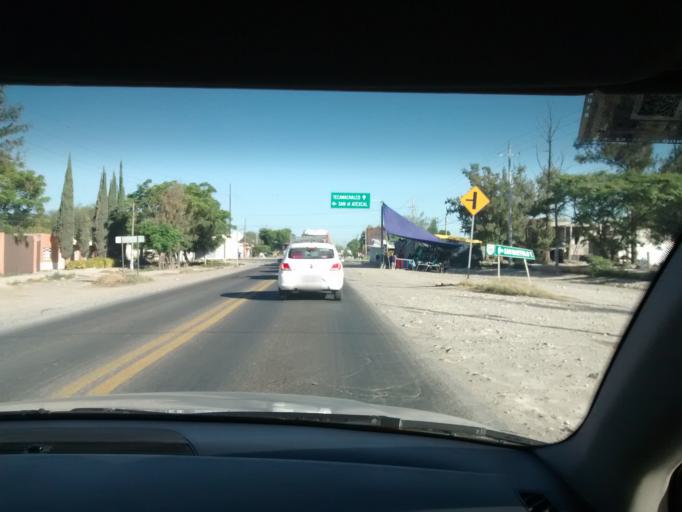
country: MX
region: Puebla
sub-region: Tehuacan
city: Magdalena Cuayucatepec
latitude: 18.5153
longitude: -97.4987
